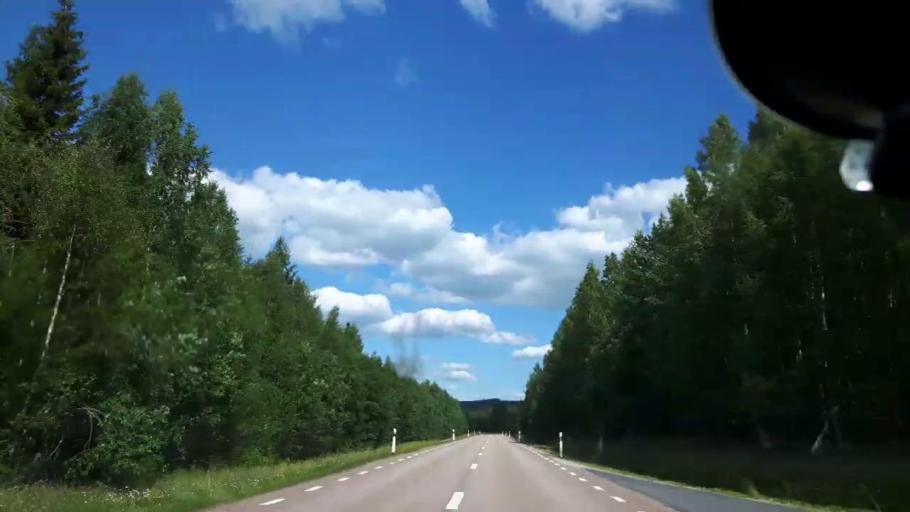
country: SE
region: Jaemtland
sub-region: Ragunda Kommun
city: Hammarstrand
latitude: 62.8952
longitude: 16.6940
